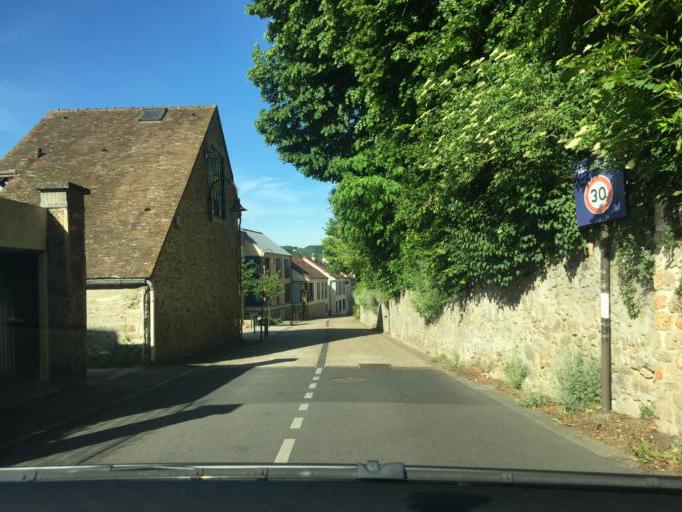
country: FR
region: Ile-de-France
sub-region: Departement de l'Essonne
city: Gif-sur-Yvette
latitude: 48.7029
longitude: 2.1370
